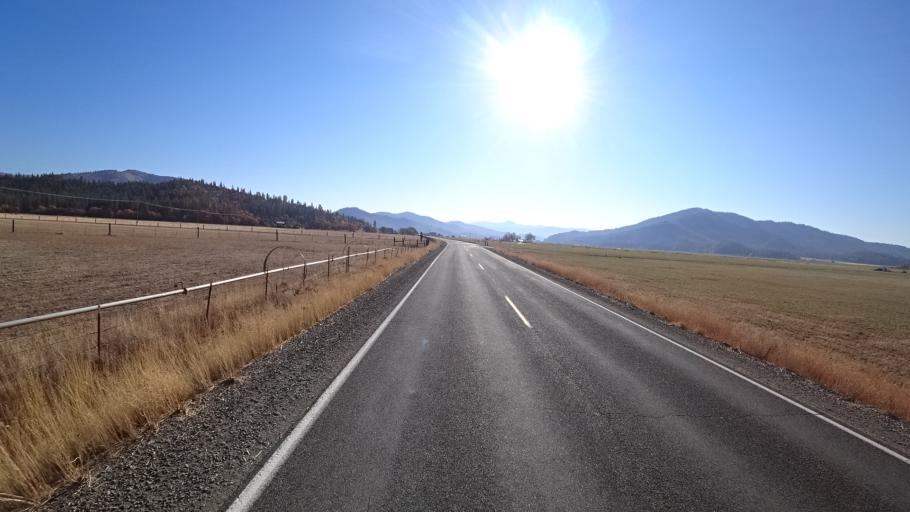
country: US
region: California
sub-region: Siskiyou County
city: Yreka
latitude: 41.6325
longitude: -122.8980
